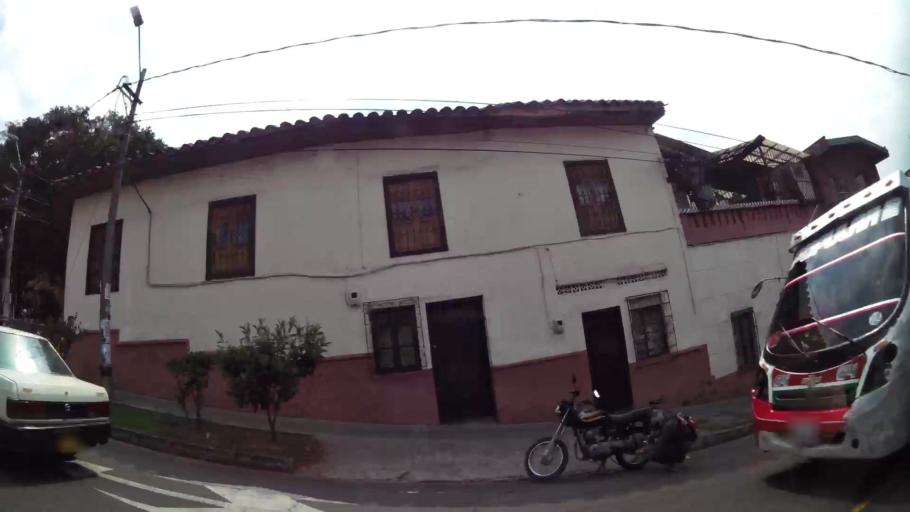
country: CO
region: Antioquia
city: Medellin
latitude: 6.2706
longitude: -75.5586
